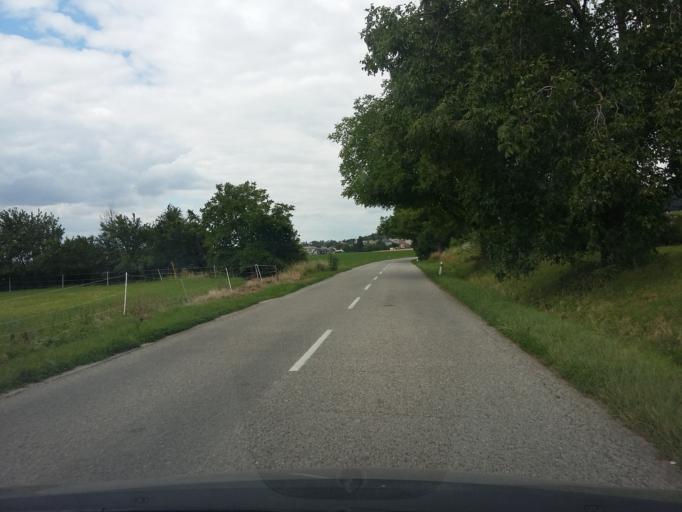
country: SK
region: Trnavsky
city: Smolenice
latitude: 48.5469
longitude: 17.3490
